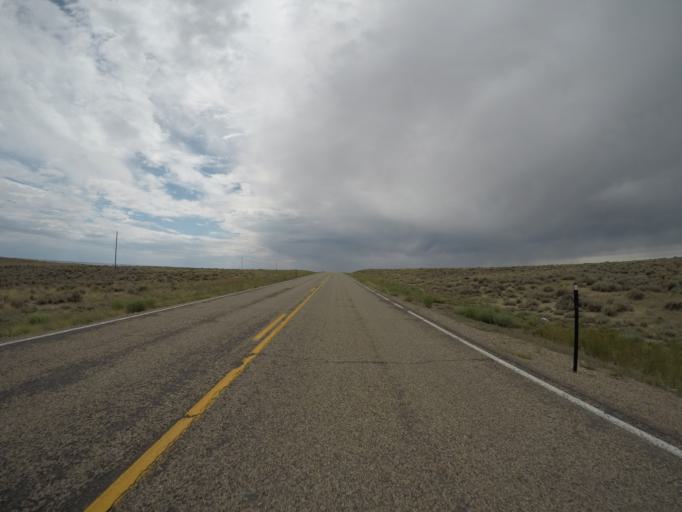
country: US
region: Wyoming
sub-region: Lincoln County
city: Kemmerer
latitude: 41.9662
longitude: -110.0933
